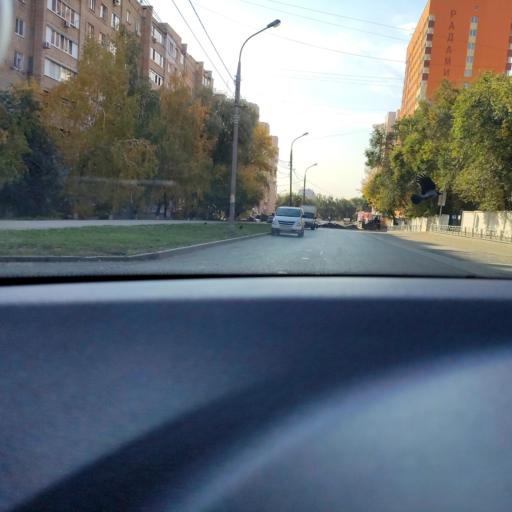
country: RU
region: Samara
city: Samara
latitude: 53.2091
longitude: 50.2207
